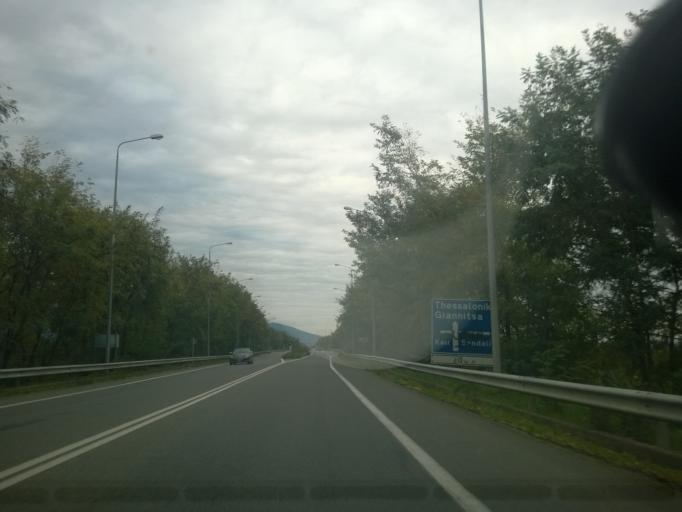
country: GR
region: Central Macedonia
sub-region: Nomos Pellis
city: Kali
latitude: 40.7985
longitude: 22.1865
